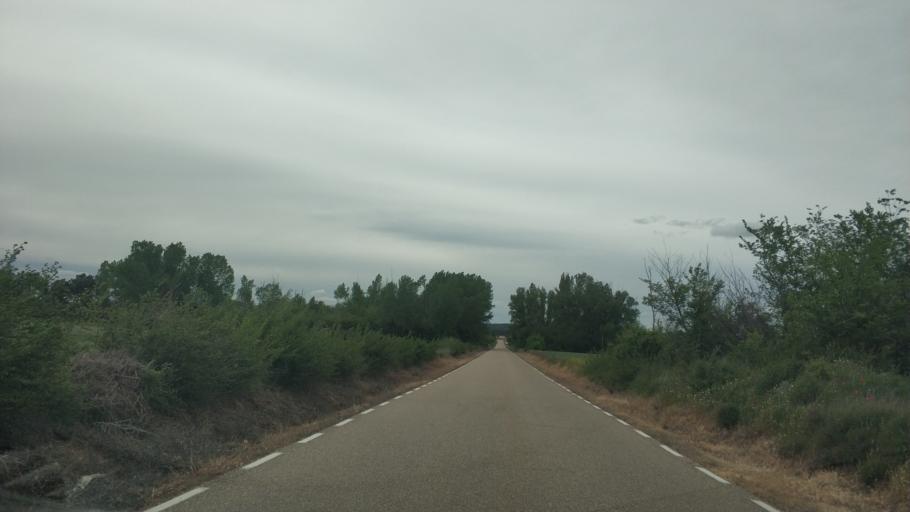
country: ES
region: Castille and Leon
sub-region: Provincia de Soria
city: Berlanga de Duero
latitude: 41.4872
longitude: -2.8664
